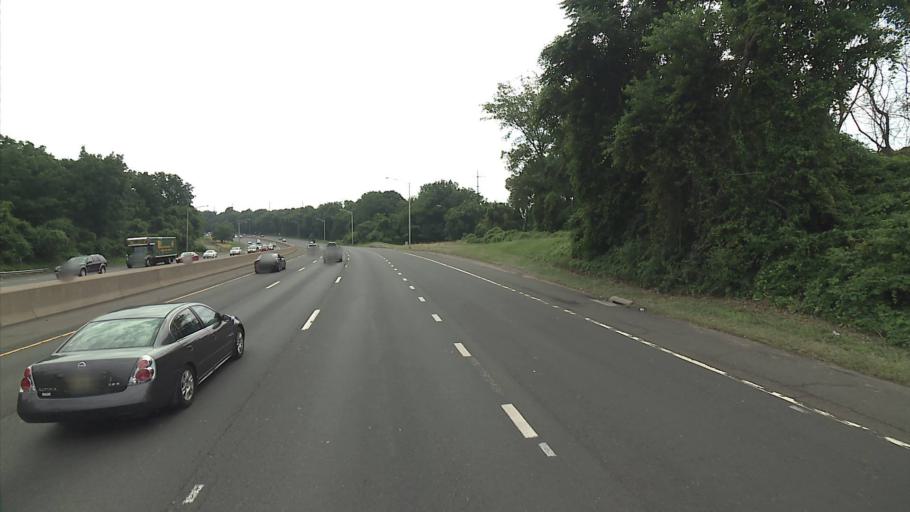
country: US
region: Connecticut
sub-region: Fairfield County
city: Westport
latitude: 41.1209
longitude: -73.3277
